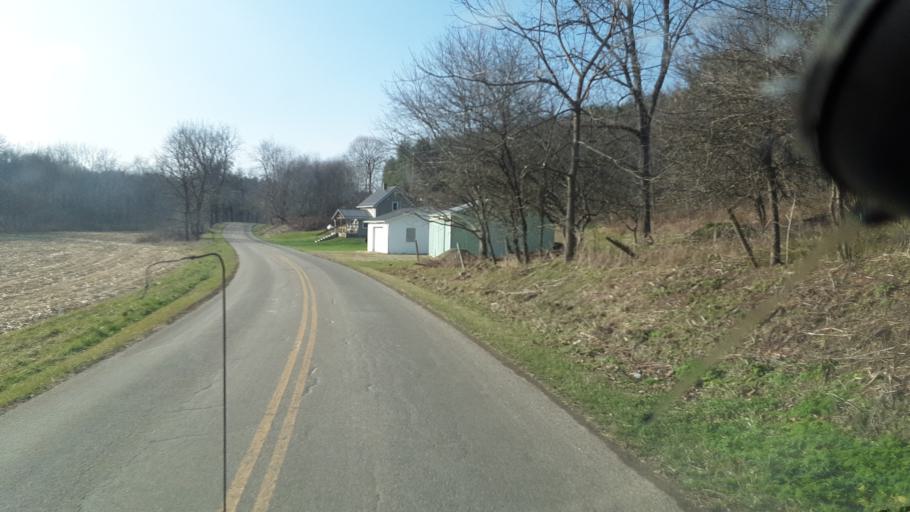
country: US
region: Ohio
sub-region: Knox County
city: Oak Hill
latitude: 40.4125
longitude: -82.2116
